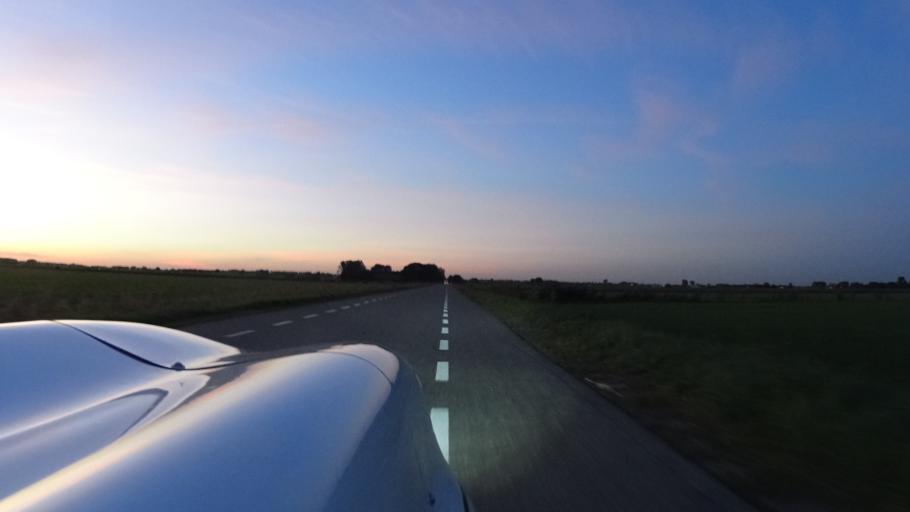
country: NL
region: North Brabant
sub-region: Gemeente Aalburg
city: Aalburg
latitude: 51.7466
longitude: 5.0853
